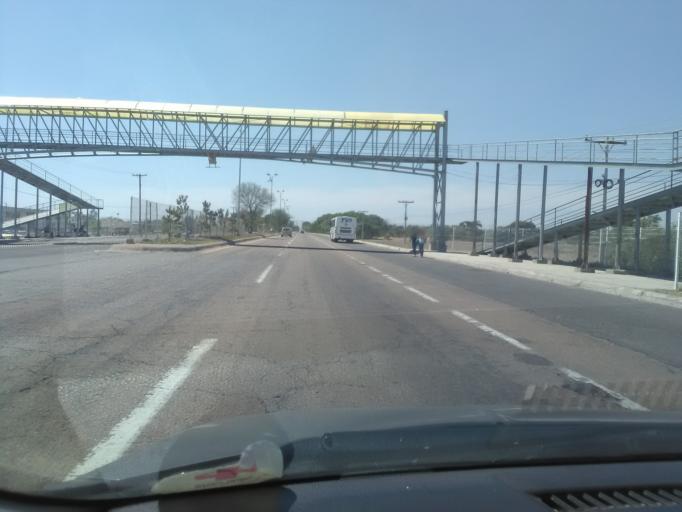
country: MX
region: Durango
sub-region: Durango
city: Jose Refugio Salcido
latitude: 24.0241
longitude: -104.5524
